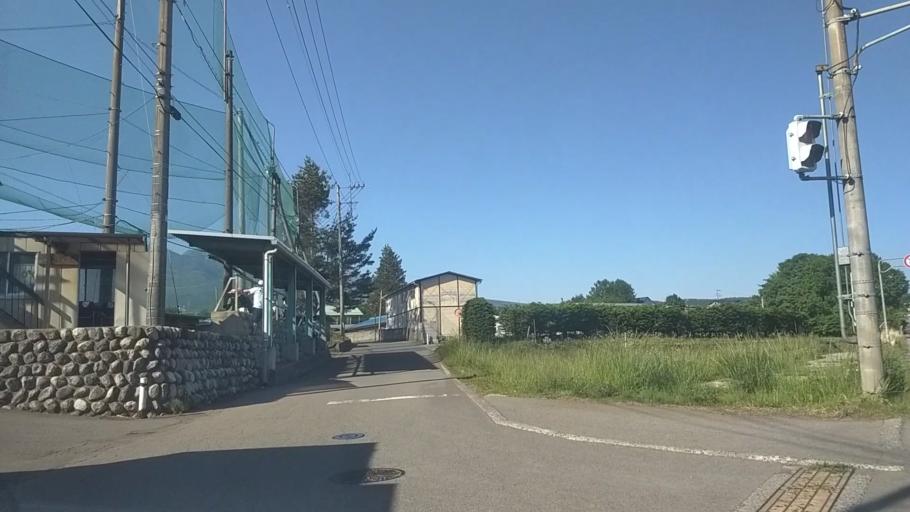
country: JP
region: Nagano
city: Chino
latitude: 35.8592
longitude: 138.3074
